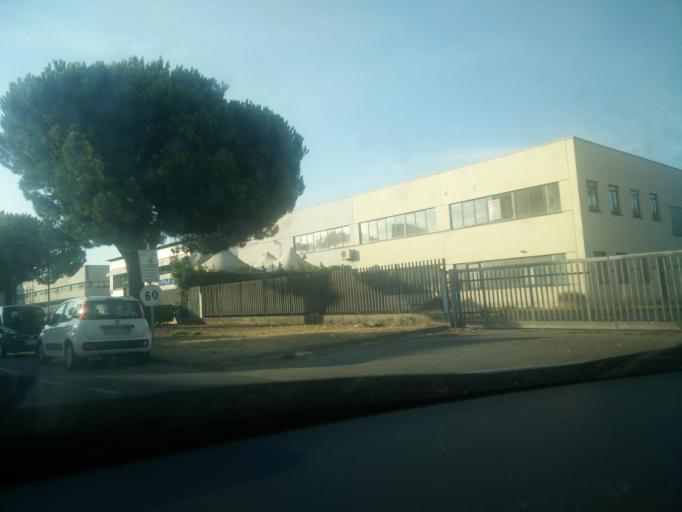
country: IT
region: Tuscany
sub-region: Provincia di Massa-Carrara
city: Massa
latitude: 44.0263
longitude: 10.1090
